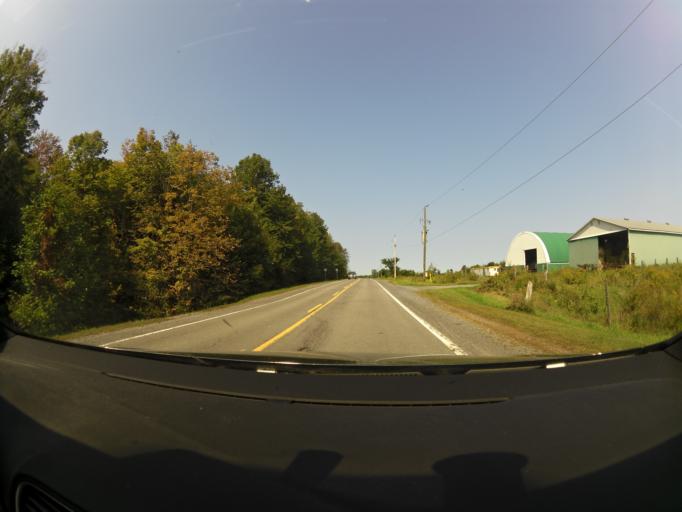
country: CA
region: Ontario
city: Arnprior
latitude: 45.4922
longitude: -76.1948
